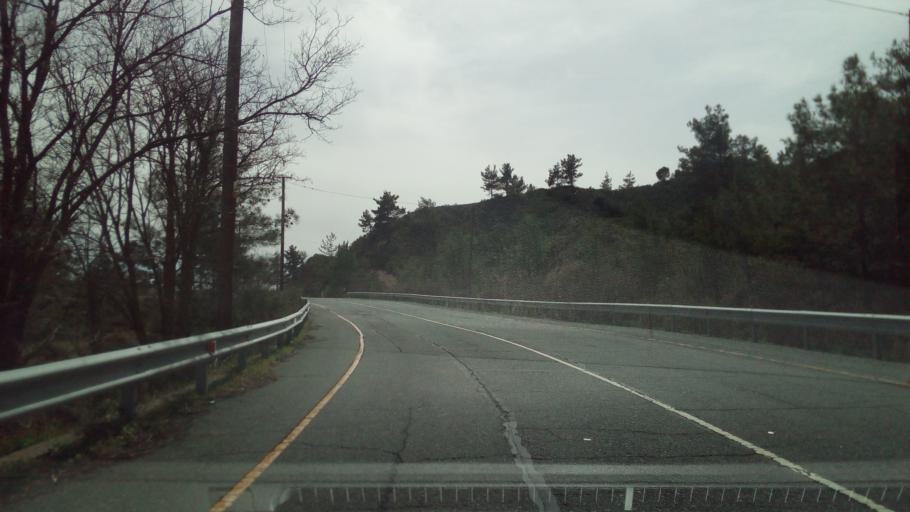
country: CY
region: Limassol
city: Pelendri
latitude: 34.8824
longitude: 32.9460
